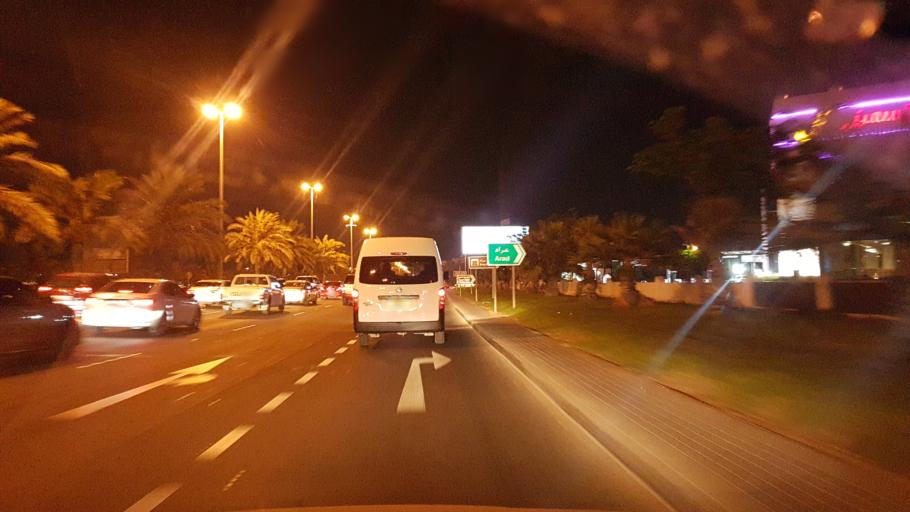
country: BH
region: Muharraq
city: Al Muharraq
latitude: 26.2592
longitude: 50.6276
